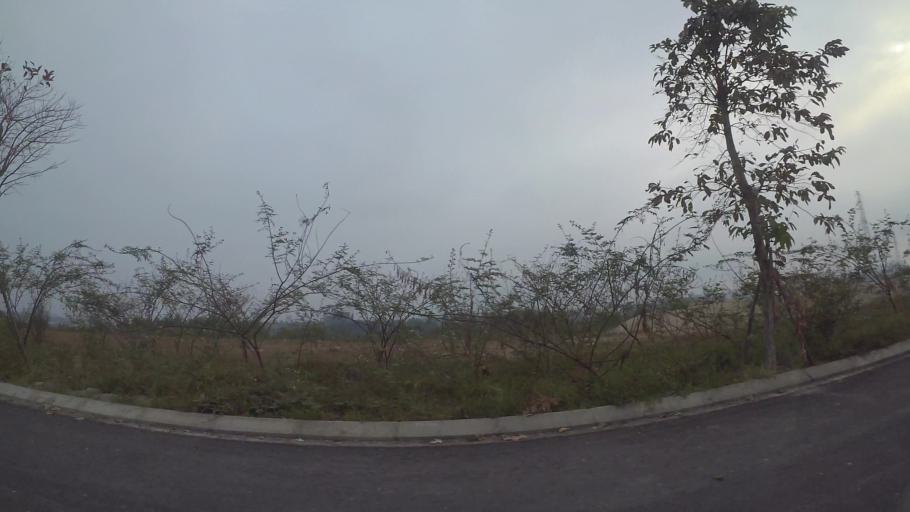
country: VN
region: Da Nang
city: Ngu Hanh Son
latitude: 16.0237
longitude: 108.2363
